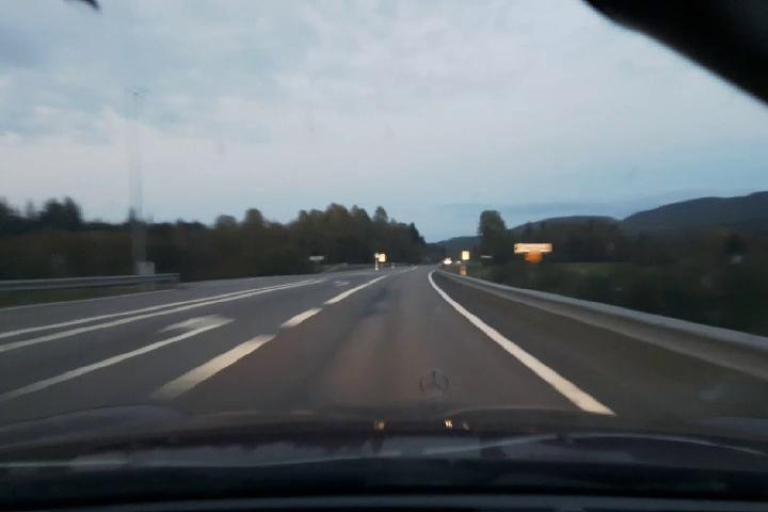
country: SE
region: Vaesternorrland
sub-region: Kramfors Kommun
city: Nordingra
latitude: 62.9609
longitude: 18.1329
